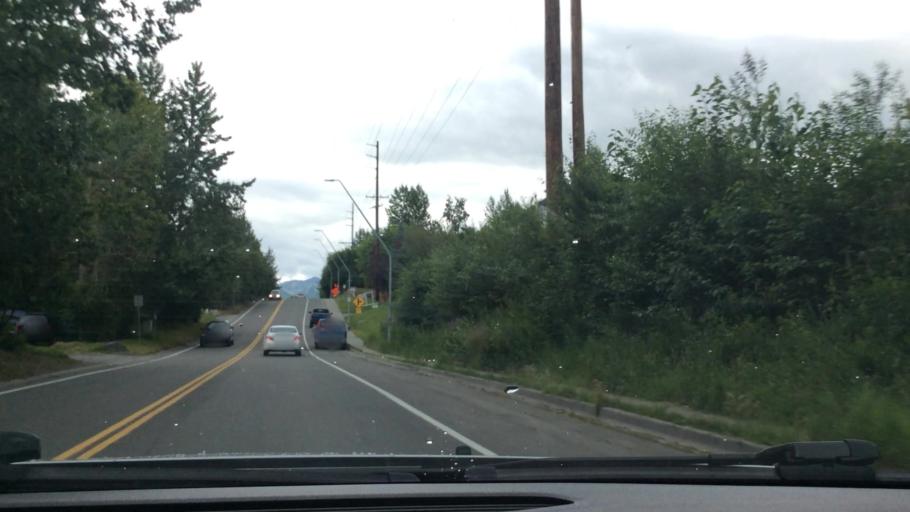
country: US
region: Alaska
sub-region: Anchorage Municipality
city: Elmendorf Air Force Base
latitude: 61.2242
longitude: -149.7403
